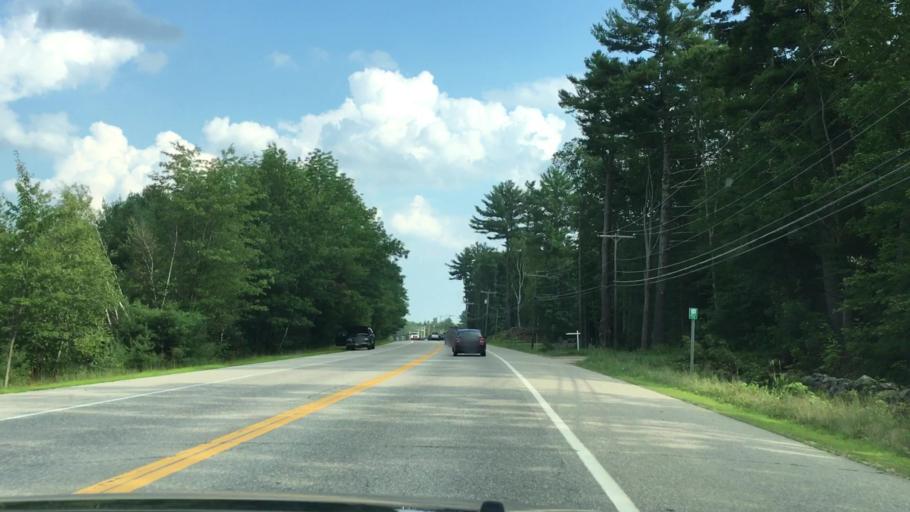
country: US
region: New Hampshire
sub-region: Strafford County
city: Farmington
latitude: 43.3474
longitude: -71.0240
